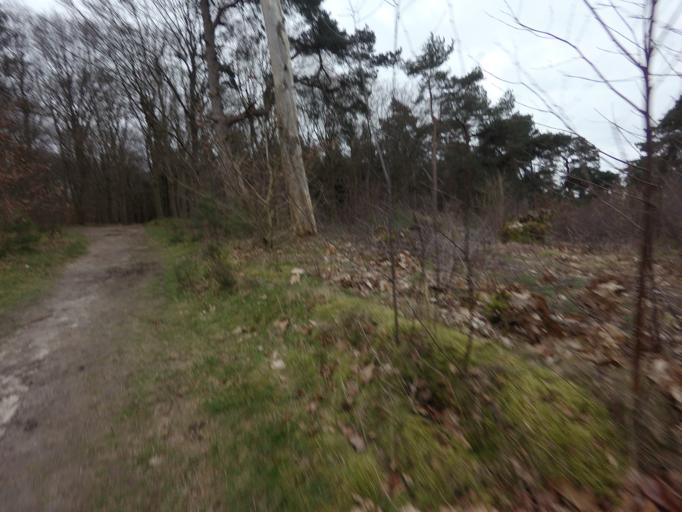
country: NL
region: Utrecht
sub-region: Gemeente Utrechtse Heuvelrug
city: Doorn
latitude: 52.0391
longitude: 5.3536
